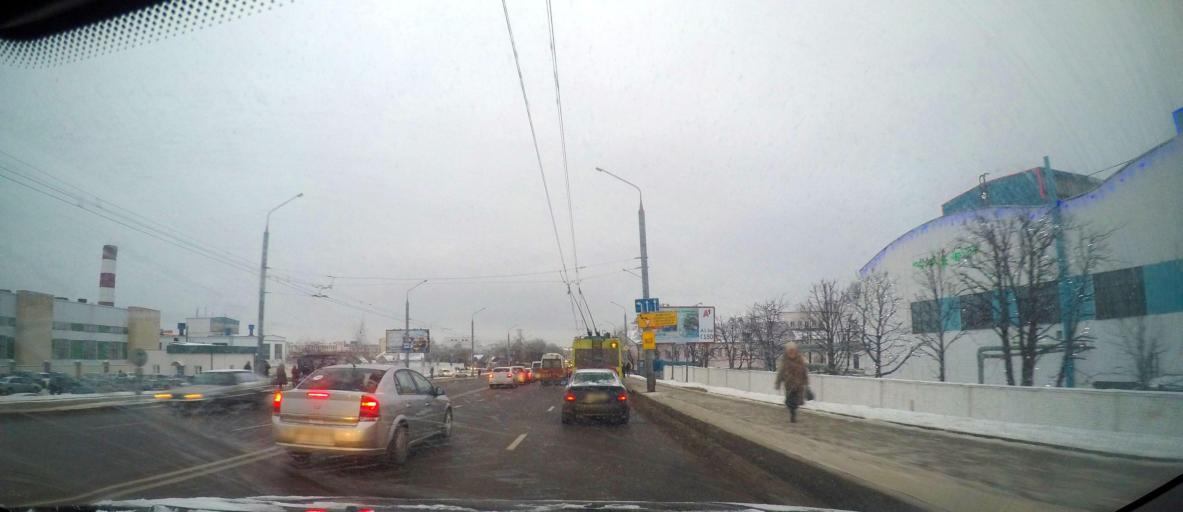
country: BY
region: Grodnenskaya
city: Hrodna
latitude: 53.6655
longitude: 23.8274
